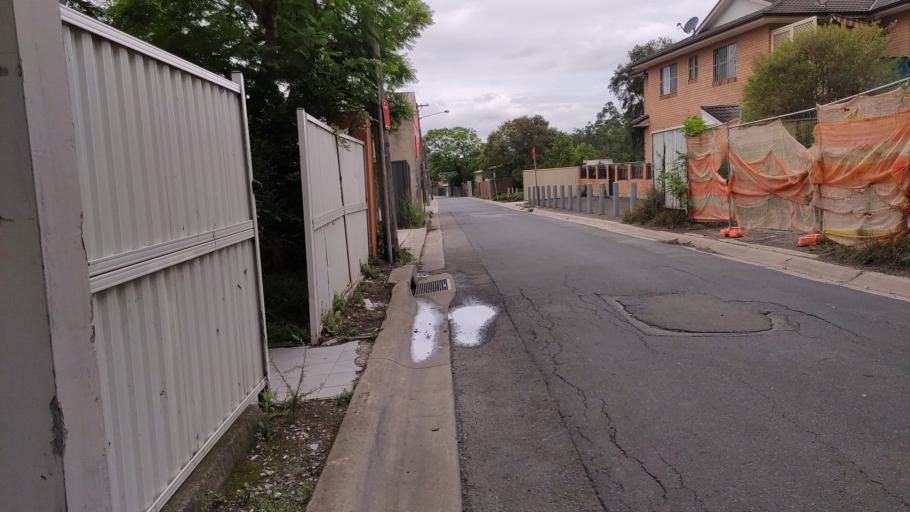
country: AU
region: New South Wales
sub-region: Strathfield
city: Homebush
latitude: -33.8643
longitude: 151.0819
